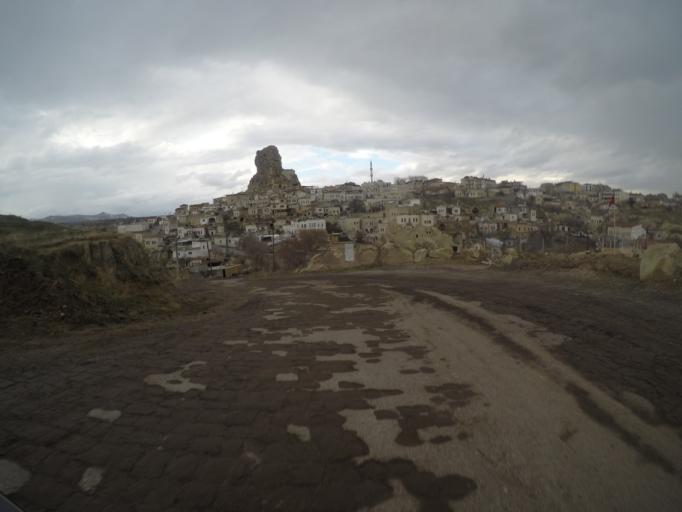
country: TR
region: Nevsehir
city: Goereme
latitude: 38.6194
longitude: 34.8678
